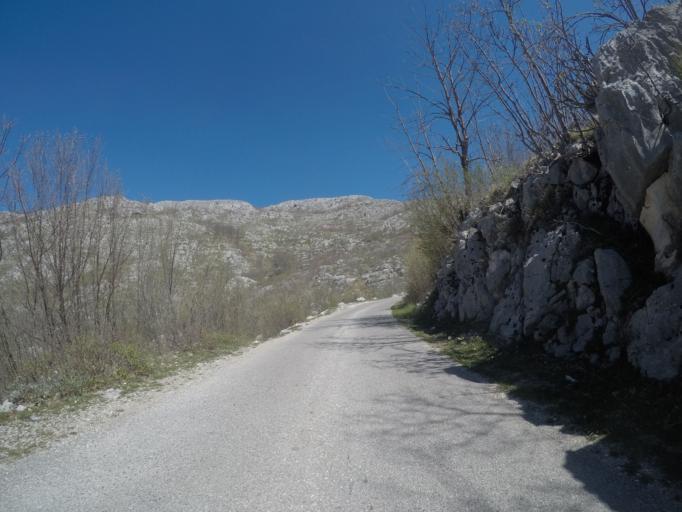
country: ME
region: Cetinje
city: Cetinje
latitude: 42.4979
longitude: 18.8791
